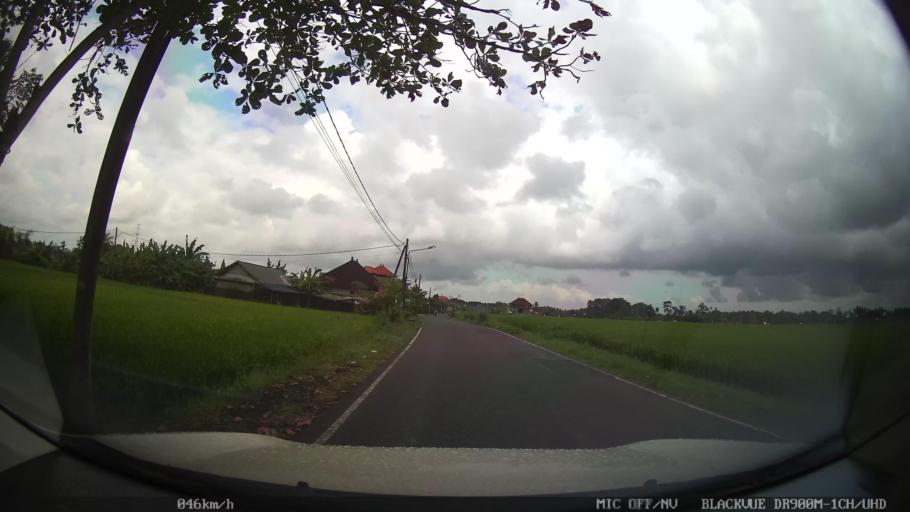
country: ID
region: Bali
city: Banjar Serangan
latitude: -8.5501
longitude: 115.1817
